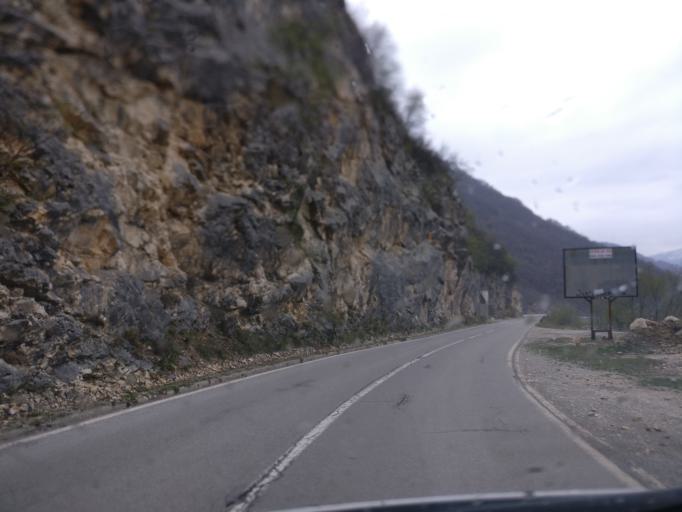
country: ME
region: Opstina Pluzine
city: Pluzine
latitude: 43.1701
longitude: 18.8587
